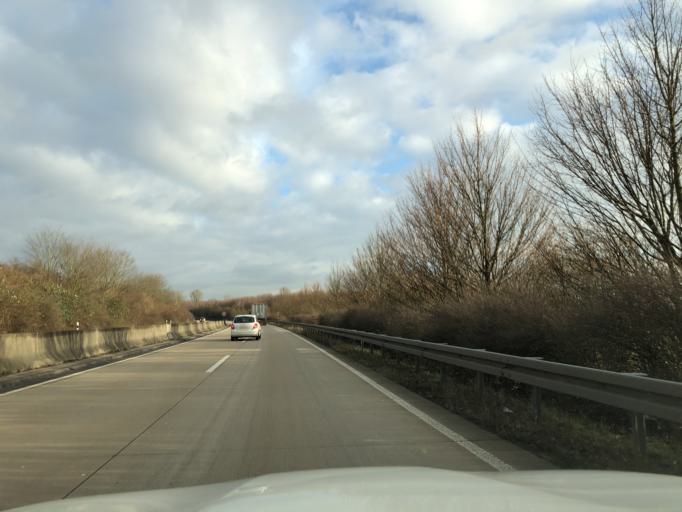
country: DE
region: North Rhine-Westphalia
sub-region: Regierungsbezirk Dusseldorf
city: Dusseldorf
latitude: 51.2972
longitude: 6.7690
